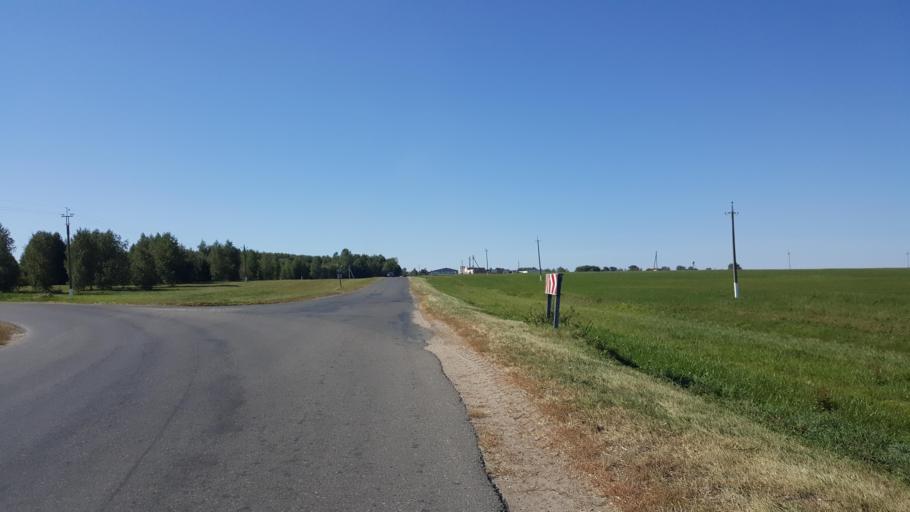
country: BY
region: Brest
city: Charnawchytsy
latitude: 52.2744
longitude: 23.5959
